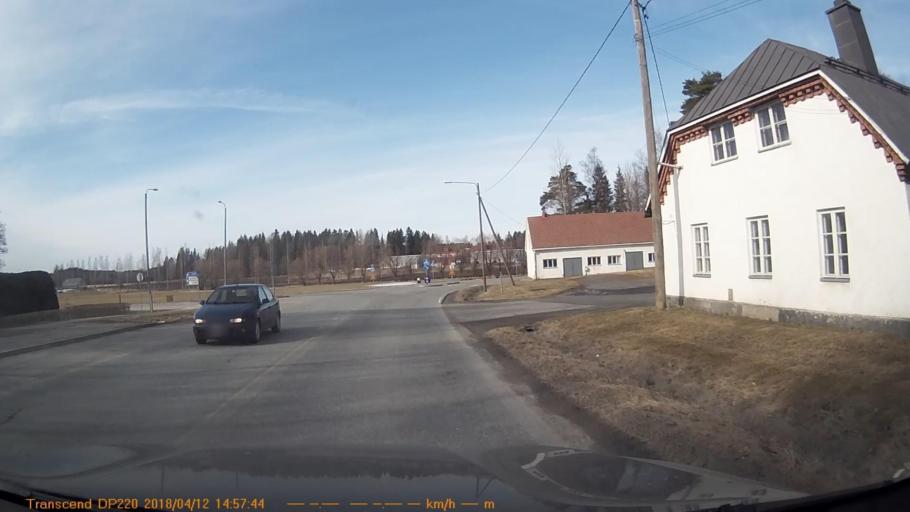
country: FI
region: Haeme
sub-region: Forssa
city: Jokioinen
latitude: 60.8055
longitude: 23.4858
